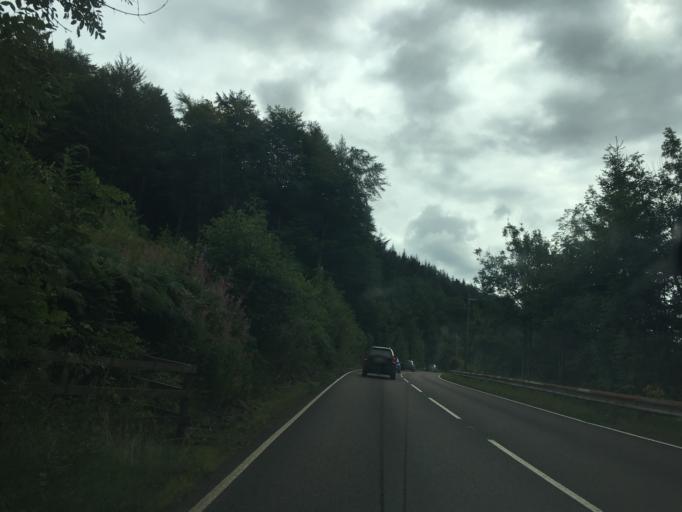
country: GB
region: Scotland
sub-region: Stirling
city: Callander
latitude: 56.2918
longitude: -4.2868
